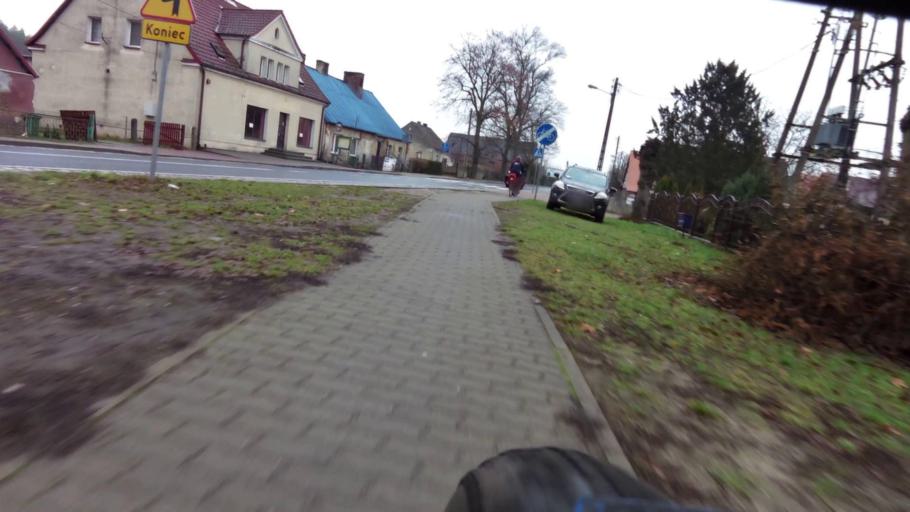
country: PL
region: Lubusz
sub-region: Powiat gorzowski
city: Kostrzyn nad Odra
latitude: 52.6205
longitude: 14.7075
